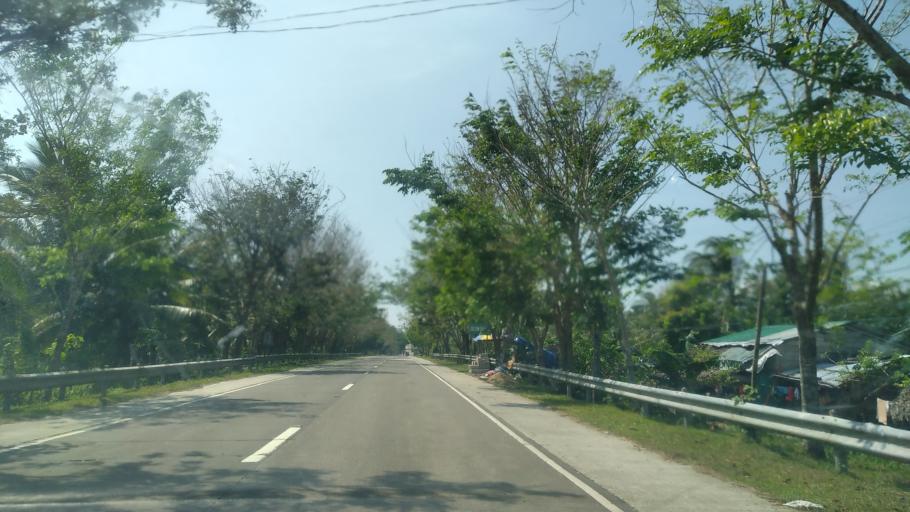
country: PH
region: Calabarzon
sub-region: Province of Quezon
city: Calilayan
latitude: 13.8576
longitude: 121.9494
